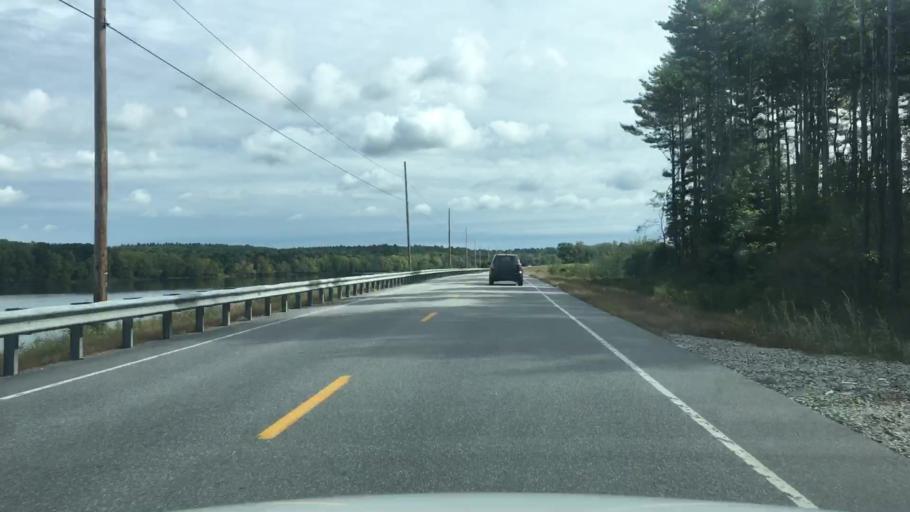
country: US
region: Maine
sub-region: Androscoggin County
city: Lisbon
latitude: 44.0010
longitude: -70.1529
